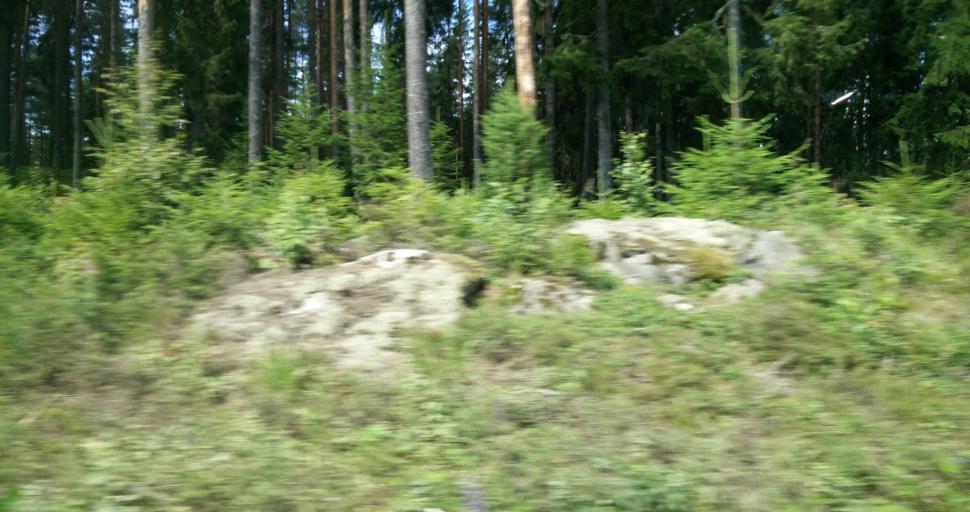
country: SE
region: Vaermland
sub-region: Hagfors Kommun
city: Ekshaerad
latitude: 60.0878
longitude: 13.4491
